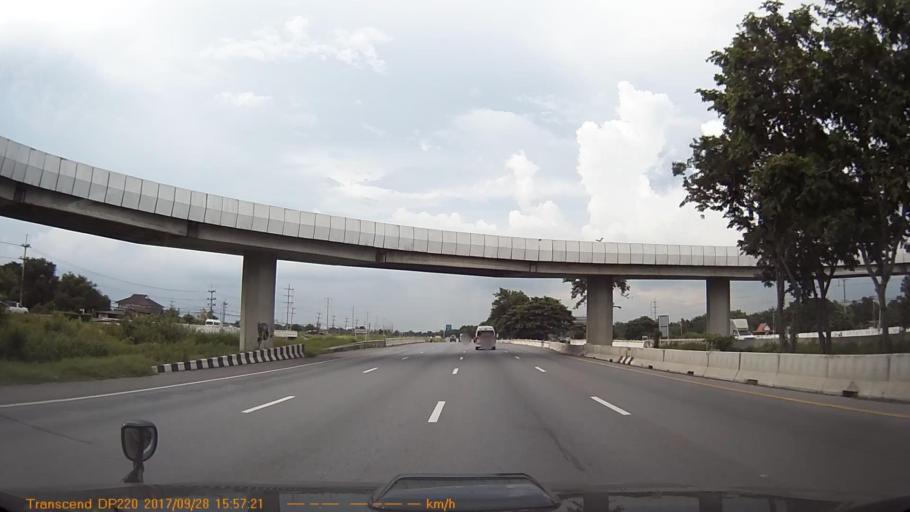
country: TH
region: Phra Nakhon Si Ayutthaya
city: Phra Nakhon Si Ayutthaya
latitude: 14.3584
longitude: 100.6128
